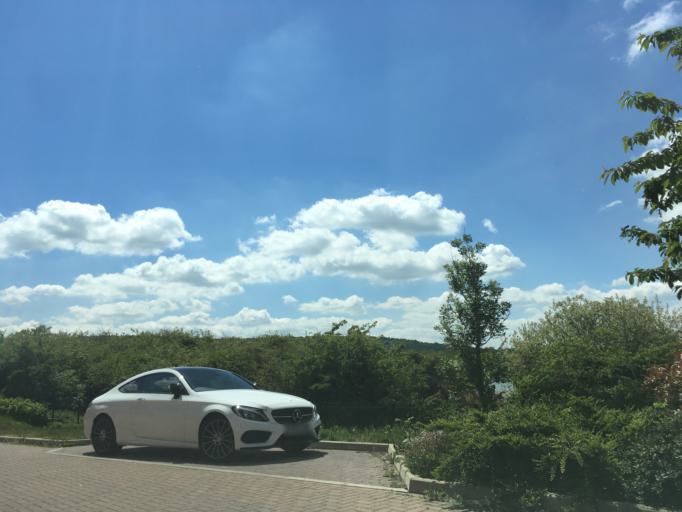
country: GB
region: England
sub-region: Milton Keynes
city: Woburn Sands
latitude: 52.0169
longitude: -0.6574
